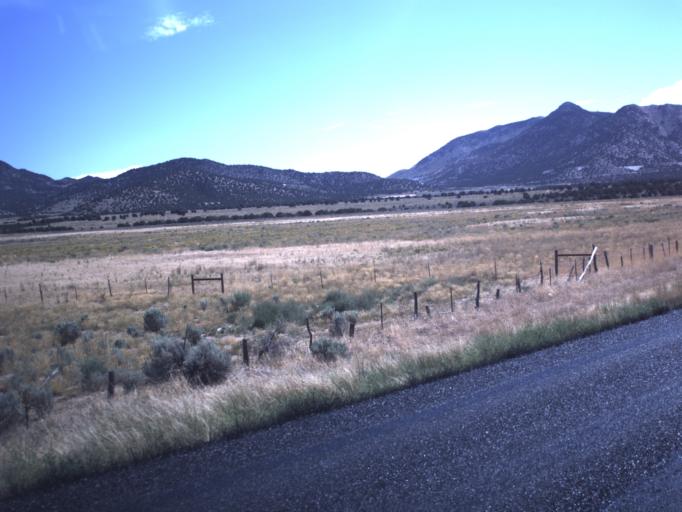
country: US
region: Utah
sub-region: Utah County
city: Genola
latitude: 39.9403
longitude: -112.1871
